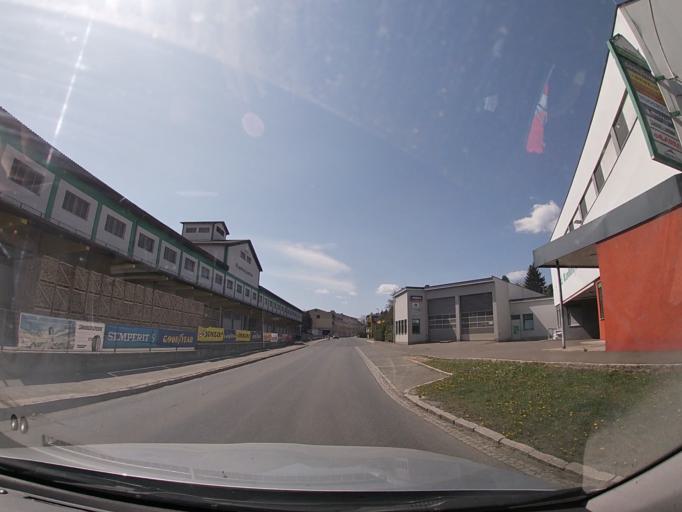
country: AT
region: Styria
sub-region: Politischer Bezirk Murtal
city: Apfelberg
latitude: 47.2178
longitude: 14.8409
